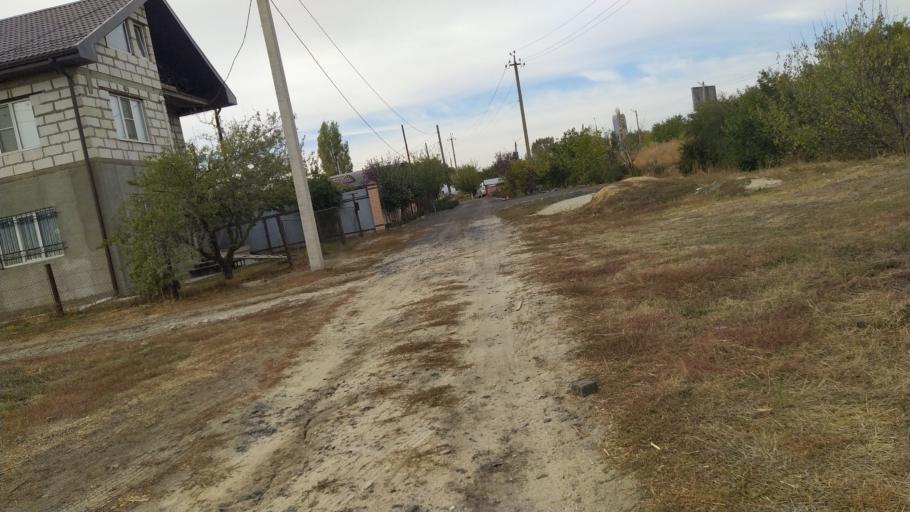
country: RU
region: Rostov
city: Bataysk
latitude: 47.1129
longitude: 39.6785
